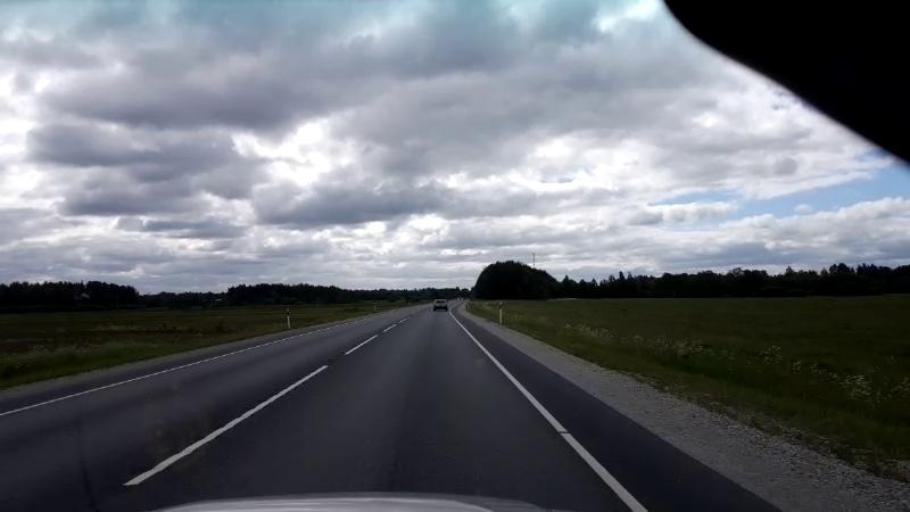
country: EE
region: Paernumaa
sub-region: Halinga vald
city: Parnu-Jaagupi
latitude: 58.6645
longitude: 24.4612
